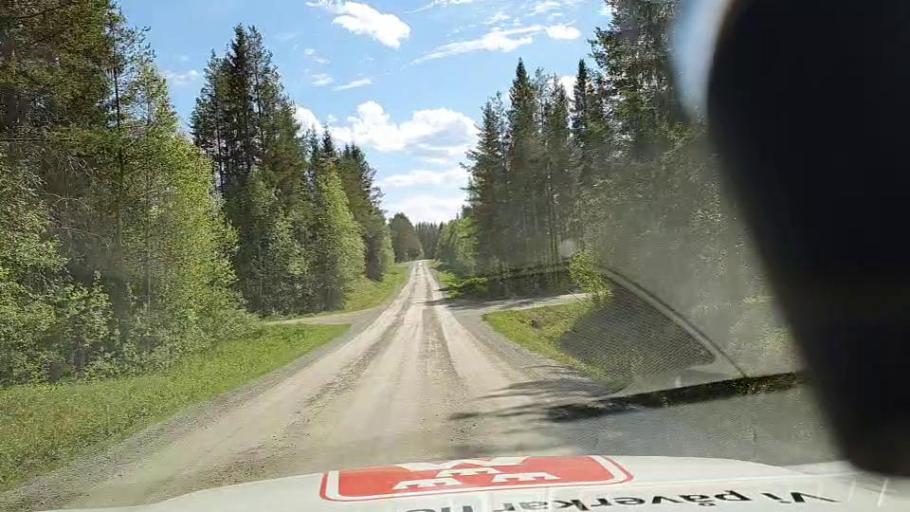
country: SE
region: Jaemtland
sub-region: Stroemsunds Kommun
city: Stroemsund
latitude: 64.4582
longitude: 15.5910
